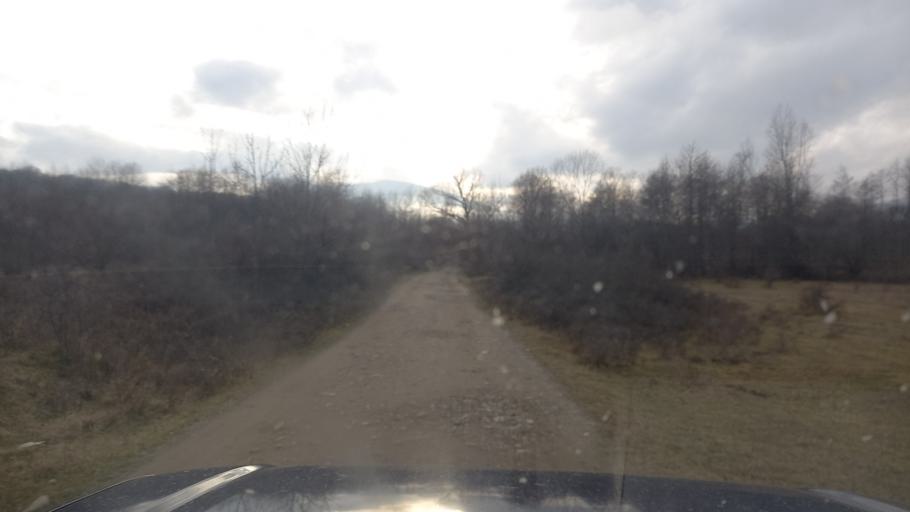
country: RU
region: Krasnodarskiy
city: Neftegorsk
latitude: 44.2420
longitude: 39.7627
